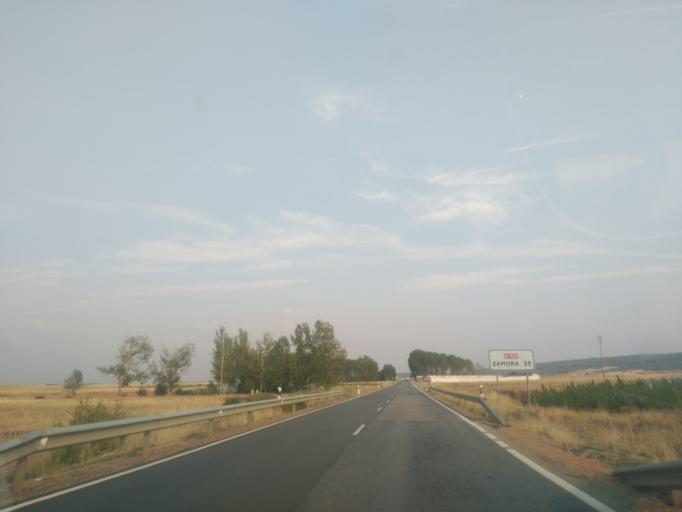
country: ES
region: Castille and Leon
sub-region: Provincia de Zamora
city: Pozuelo de Tabara
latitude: 41.7826
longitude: -5.8919
